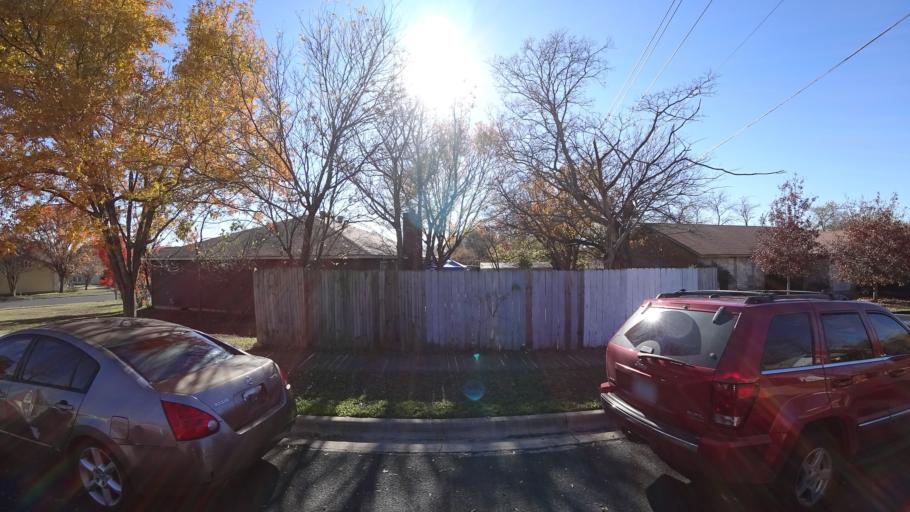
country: US
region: Texas
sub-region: Travis County
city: Wells Branch
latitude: 30.4184
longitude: -97.6930
